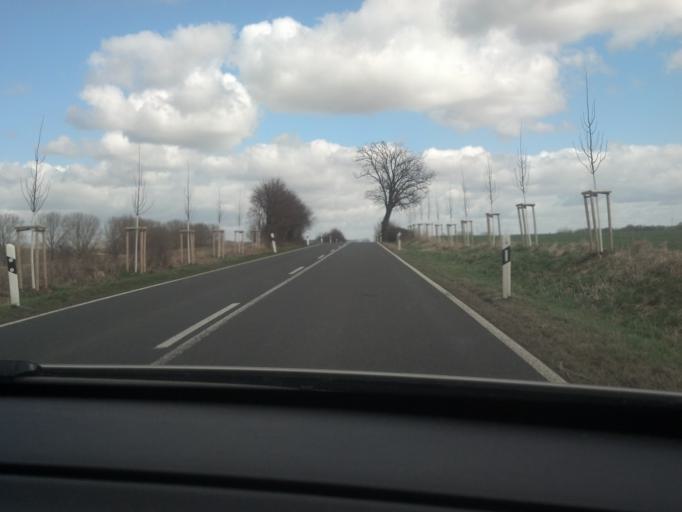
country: DE
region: Mecklenburg-Vorpommern
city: Blankensee
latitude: 53.3765
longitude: 13.3128
